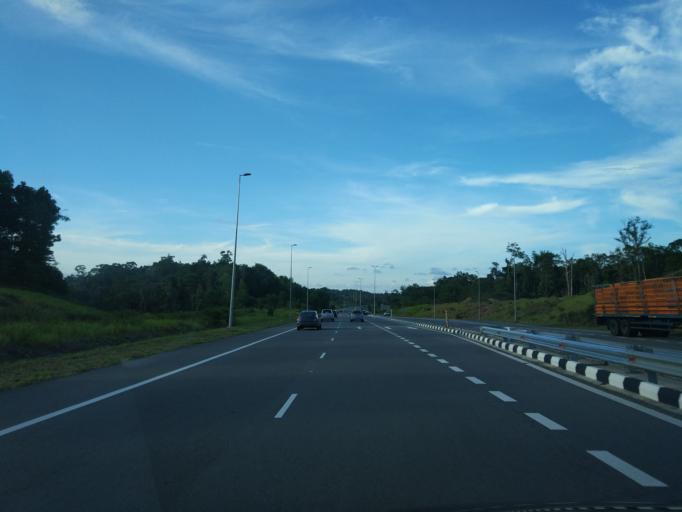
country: BN
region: Tutong
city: Tutong
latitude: 4.6569
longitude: 114.5170
